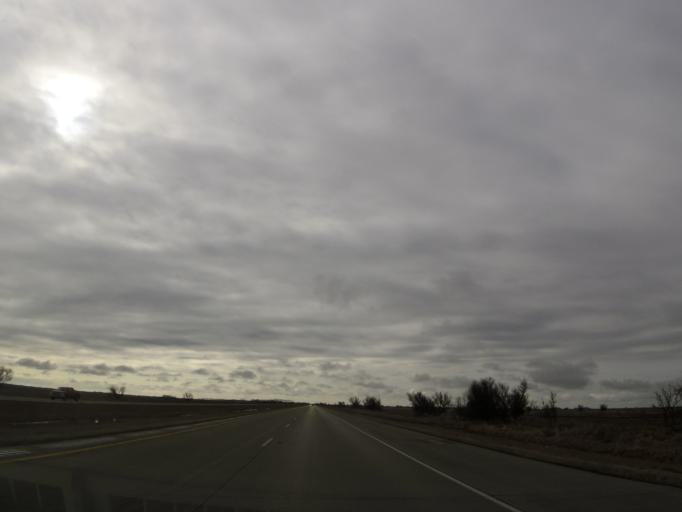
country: US
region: North Dakota
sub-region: Grand Forks County
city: Grand Forks
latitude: 48.0456
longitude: -97.1480
